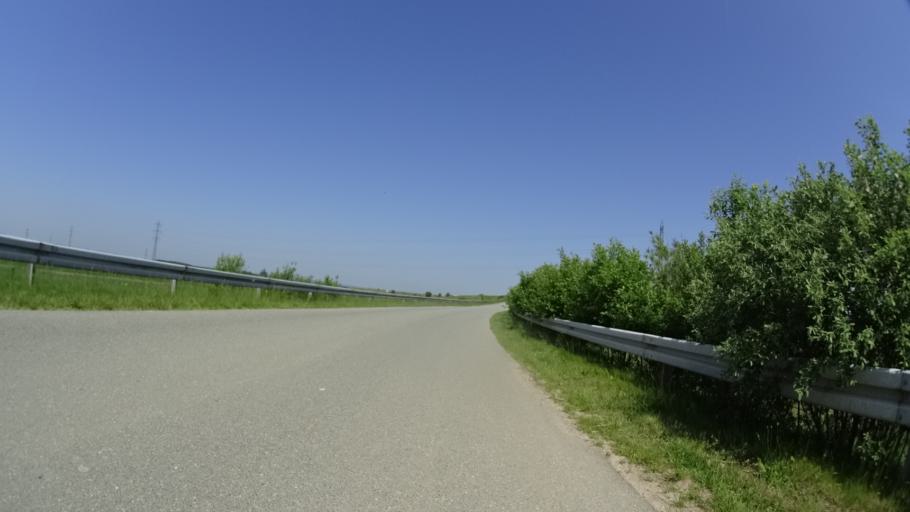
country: DK
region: Central Jutland
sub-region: Arhus Kommune
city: Kolt
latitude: 56.1192
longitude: 10.0513
